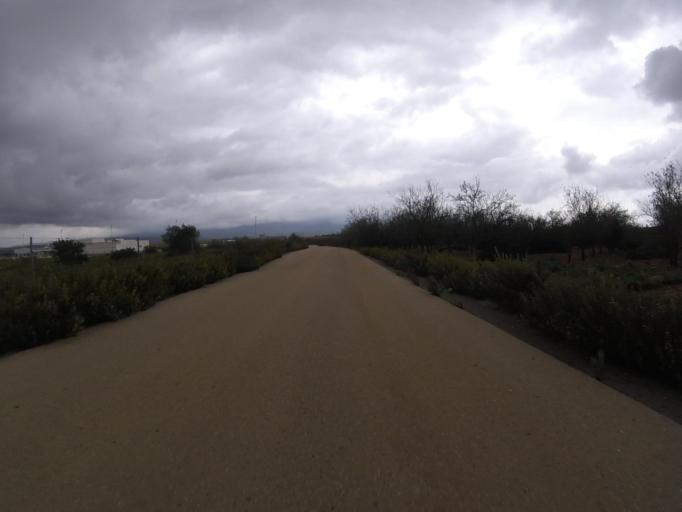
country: ES
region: Valencia
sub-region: Provincia de Castello
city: Benlloch
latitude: 40.2046
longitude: 0.0719
